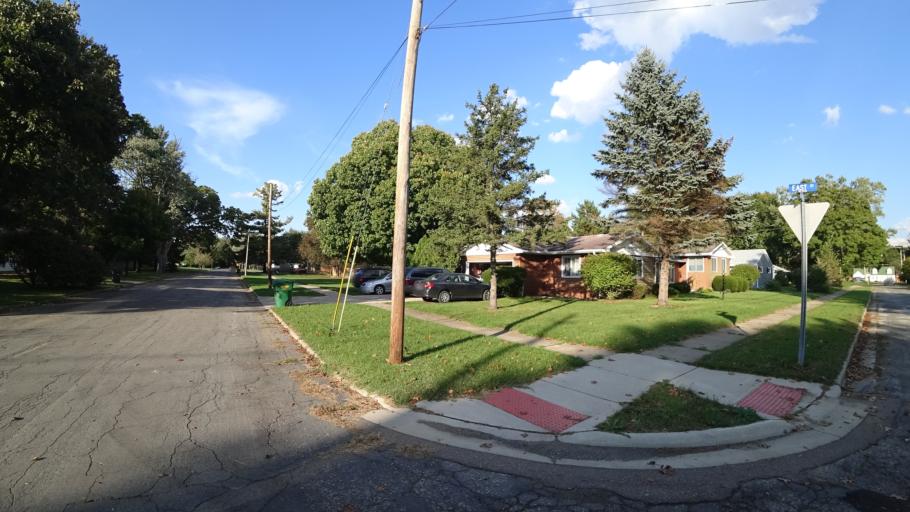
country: US
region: Michigan
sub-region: Saint Joseph County
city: Three Rivers
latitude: 41.9560
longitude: -85.6333
